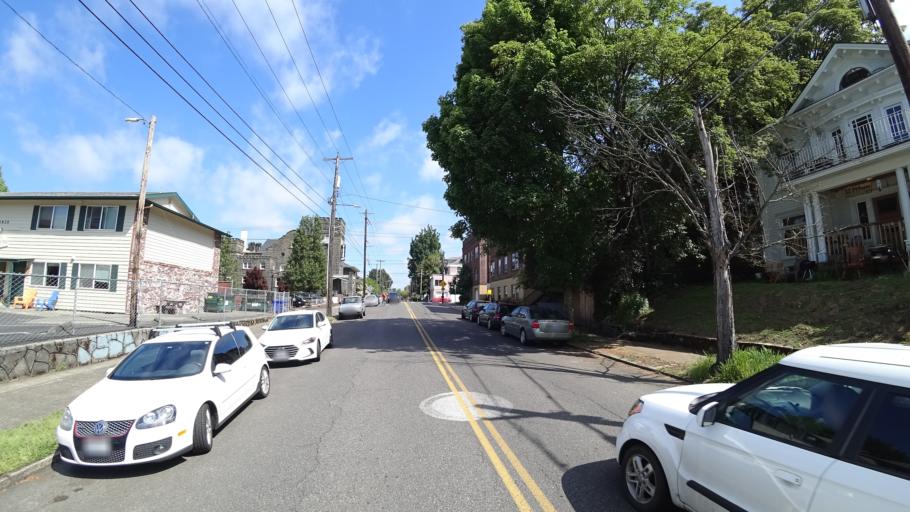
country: US
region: Oregon
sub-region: Multnomah County
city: Portland
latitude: 45.5137
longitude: -122.6456
